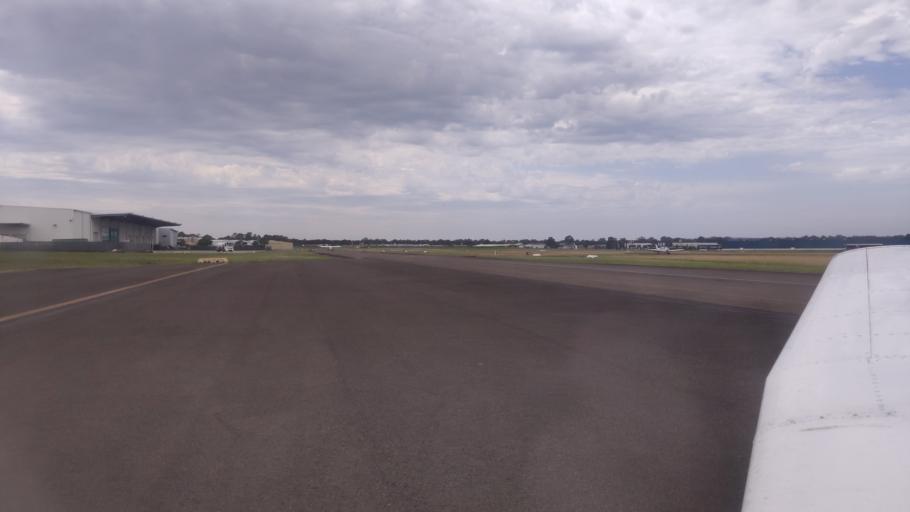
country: AU
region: New South Wales
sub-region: Bankstown
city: Milperra
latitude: -33.9220
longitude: 150.9918
